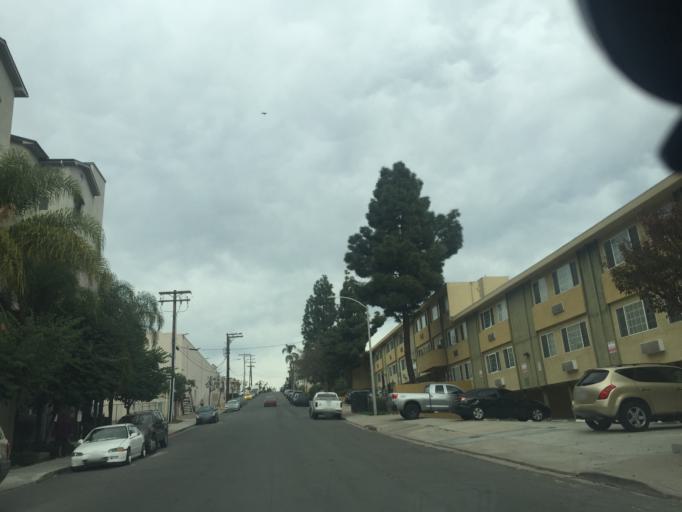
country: US
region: California
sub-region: San Diego County
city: Lemon Grove
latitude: 32.7552
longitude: -117.0826
